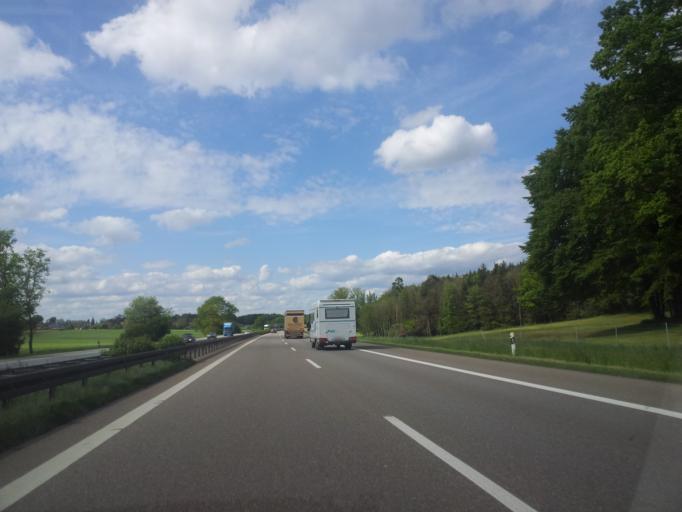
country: DE
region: Bavaria
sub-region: Swabia
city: Altenstadt
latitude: 48.1944
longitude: 10.1236
